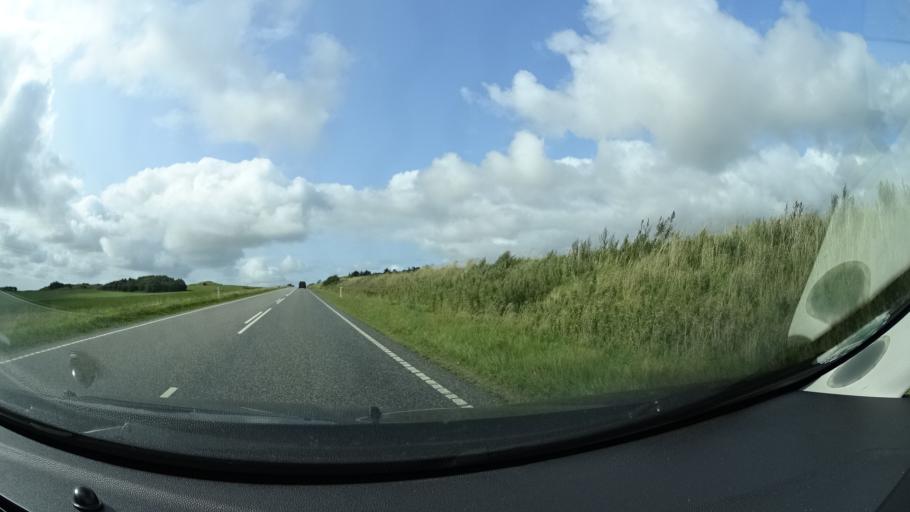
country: DK
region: Central Jutland
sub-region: Lemvig Kommune
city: Harboore
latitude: 56.5779
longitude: 8.2054
